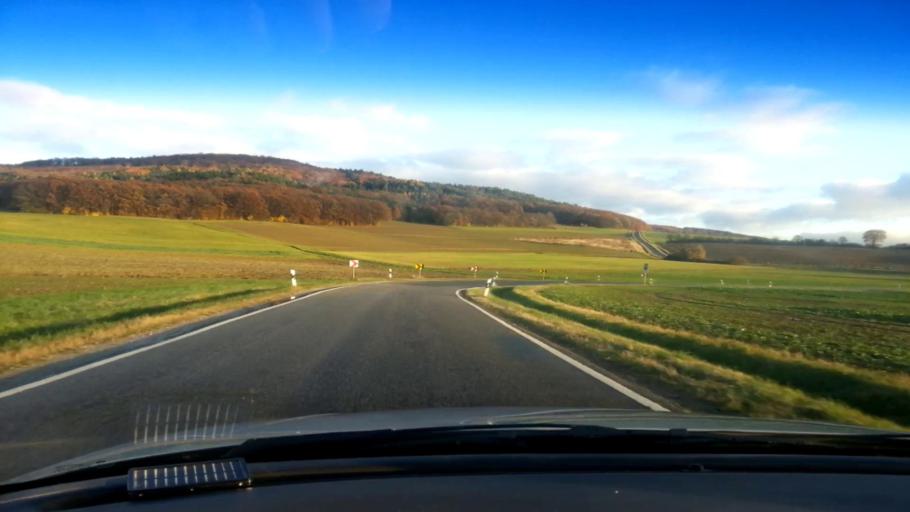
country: DE
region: Bavaria
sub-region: Upper Franconia
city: Hirschaid
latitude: 49.8501
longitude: 11.0199
